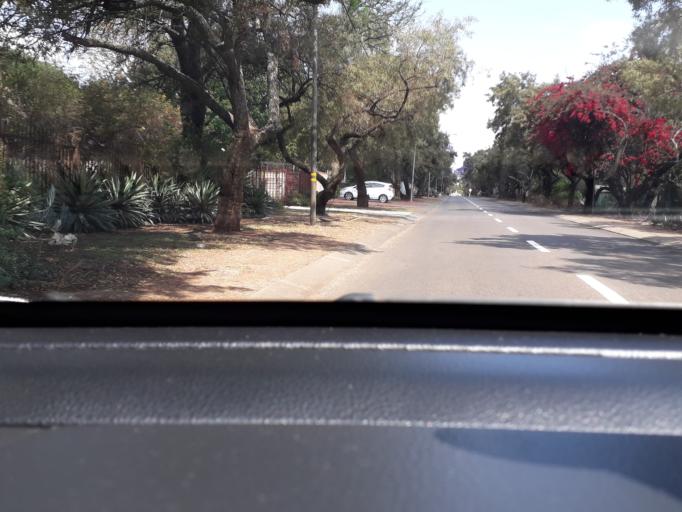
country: ZA
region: Gauteng
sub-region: City of Tshwane Metropolitan Municipality
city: Centurion
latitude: -25.8321
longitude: 28.2114
